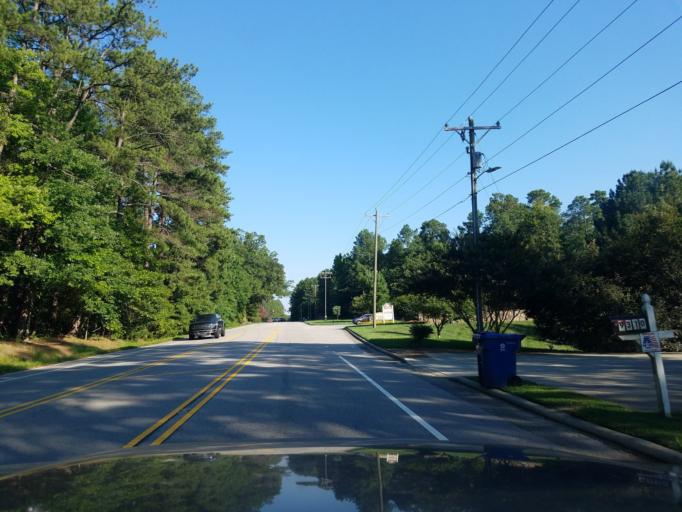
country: US
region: North Carolina
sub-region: Wake County
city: Green Level
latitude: 35.8769
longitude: -78.9513
